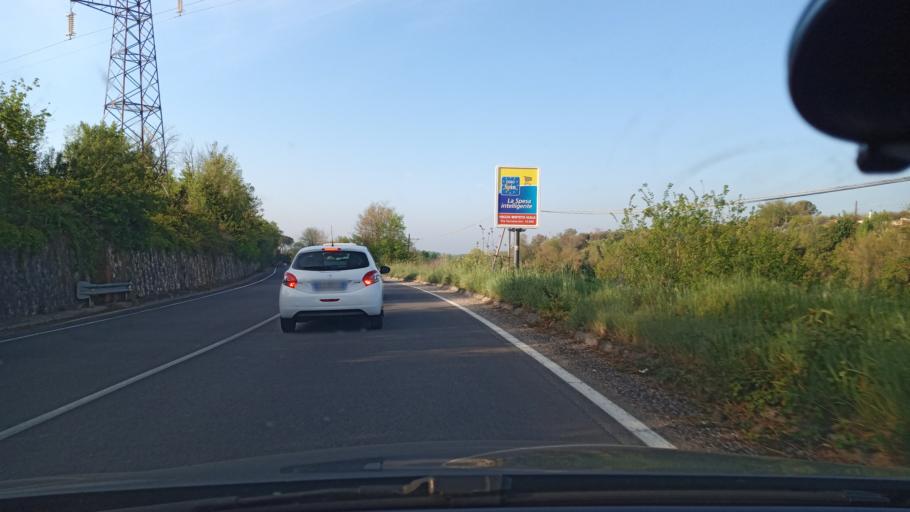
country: IT
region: Latium
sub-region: Citta metropolitana di Roma Capitale
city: Fiano Romano
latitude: 42.1760
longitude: 12.6366
